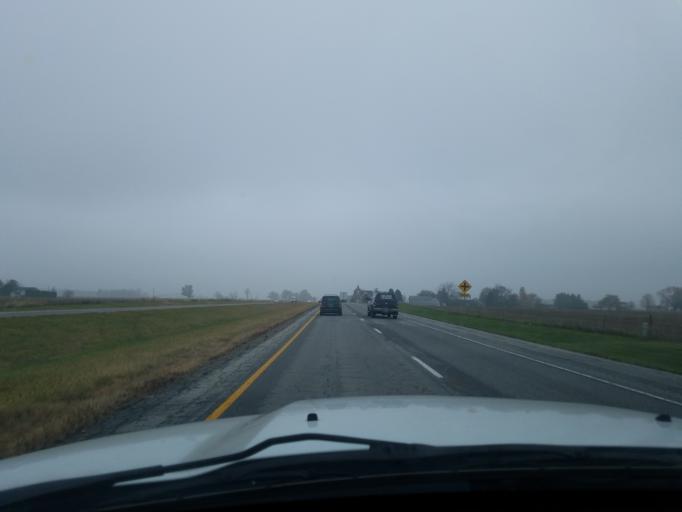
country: US
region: Indiana
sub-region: Tipton County
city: Tipton
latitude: 40.3138
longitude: -86.1269
